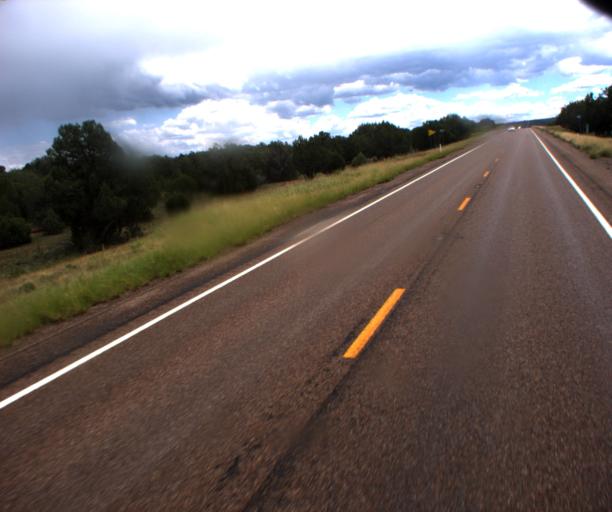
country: US
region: Arizona
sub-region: Navajo County
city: Linden
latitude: 34.3598
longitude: -110.3225
